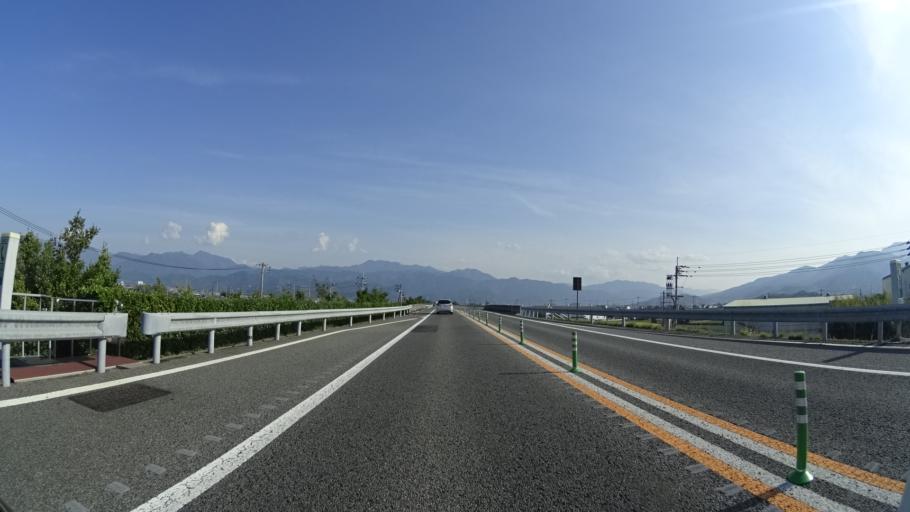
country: JP
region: Ehime
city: Saijo
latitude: 33.9408
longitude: 133.0688
